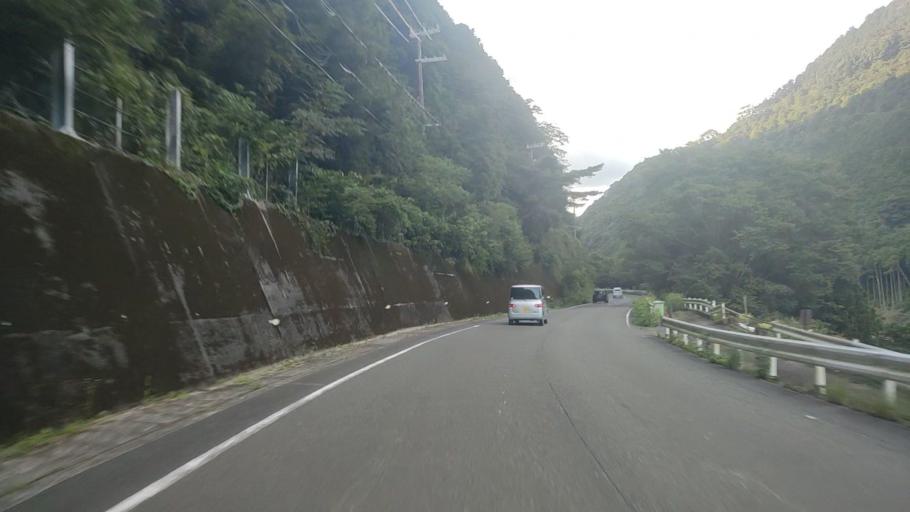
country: JP
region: Wakayama
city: Tanabe
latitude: 33.7676
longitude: 135.4997
